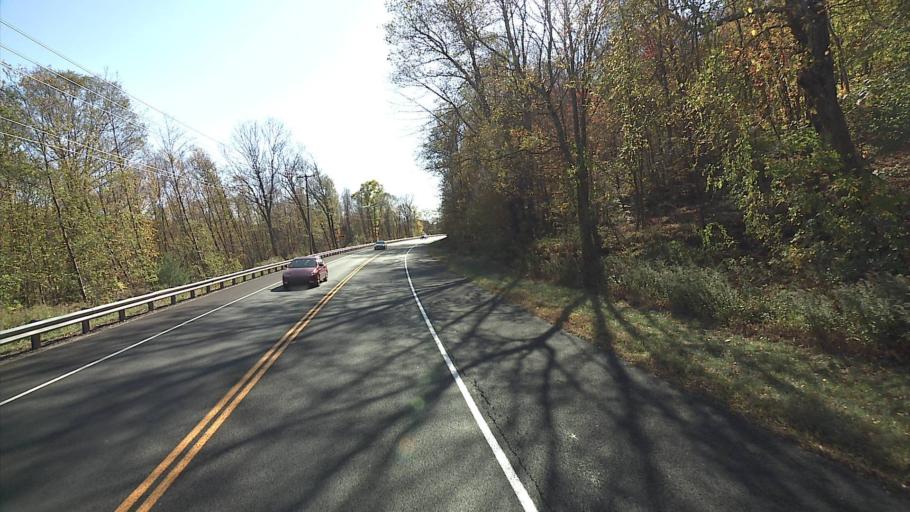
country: US
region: Connecticut
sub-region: Tolland County
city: Coventry Lake
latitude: 41.7707
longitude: -72.4090
